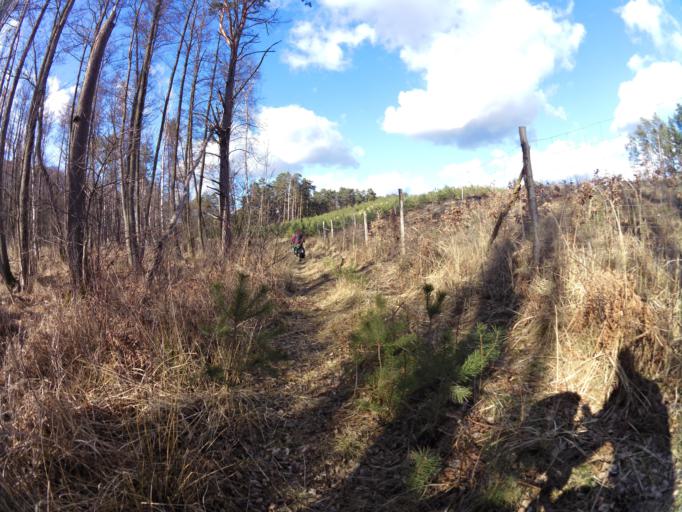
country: PL
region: West Pomeranian Voivodeship
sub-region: Powiat mysliborski
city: Debno
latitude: 52.7734
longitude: 14.7360
